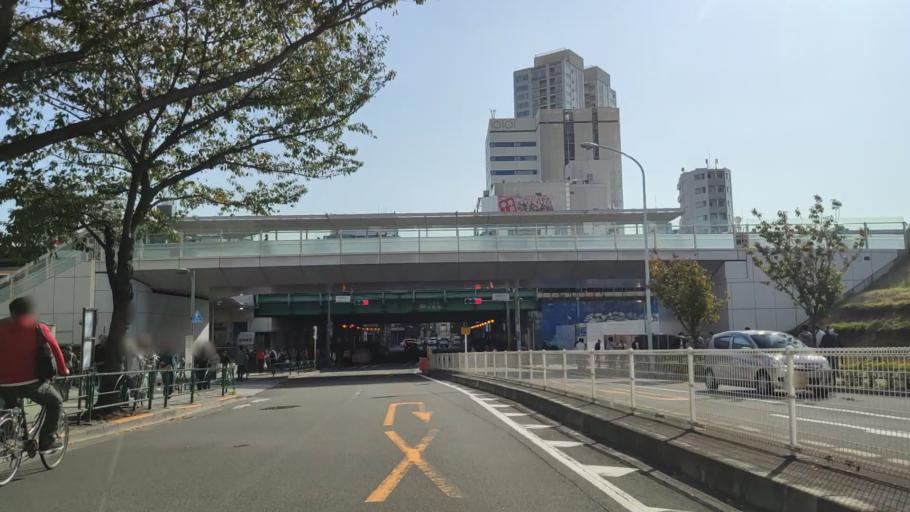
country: JP
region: Tokyo
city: Tokyo
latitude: 35.7066
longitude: 139.6653
